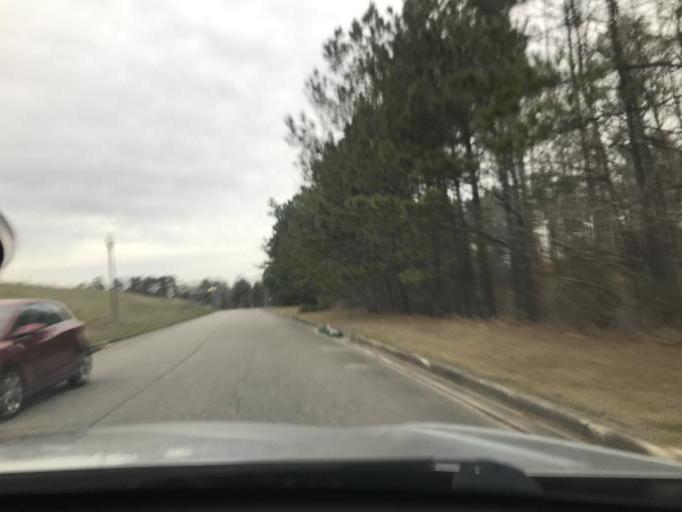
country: US
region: Alabama
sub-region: Jefferson County
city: Cahaba Heights
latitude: 33.4717
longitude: -86.6933
